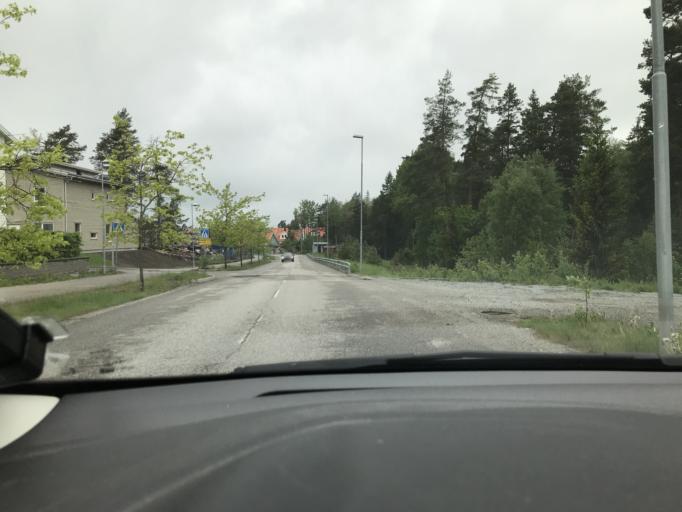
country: SE
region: Stockholm
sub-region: Botkyrka Kommun
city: Tumba
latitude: 59.2097
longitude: 17.8399
